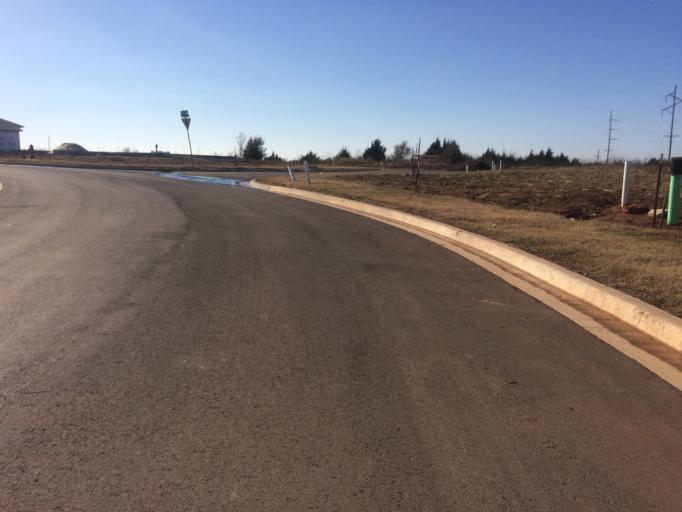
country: US
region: Oklahoma
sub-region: Cleveland County
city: Norman
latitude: 35.2541
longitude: -97.4562
